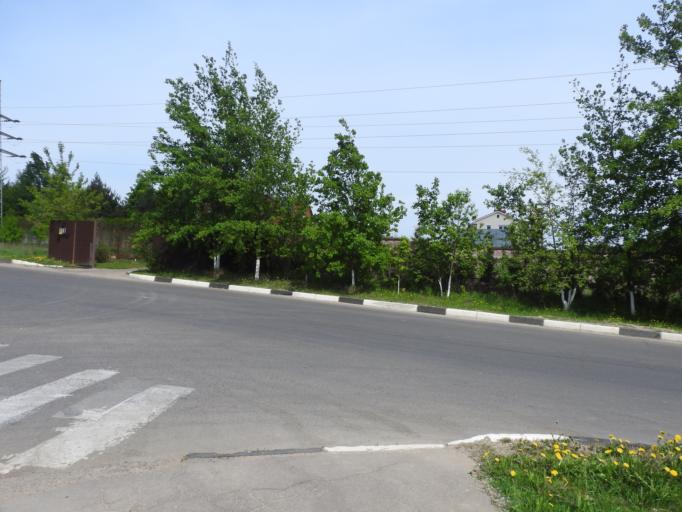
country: RU
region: Moskovskaya
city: Odintsovo
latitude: 55.6671
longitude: 37.2957
